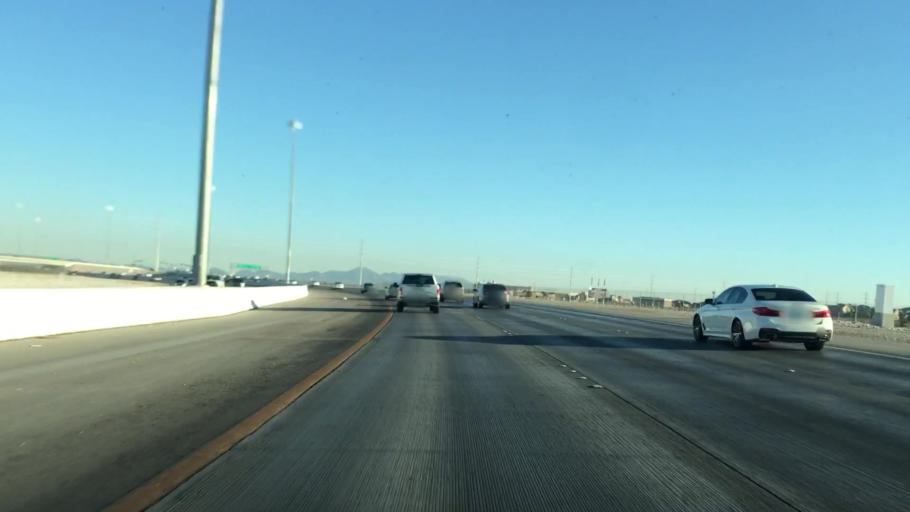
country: US
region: Nevada
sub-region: Clark County
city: Spring Valley
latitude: 36.0675
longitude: -115.2863
